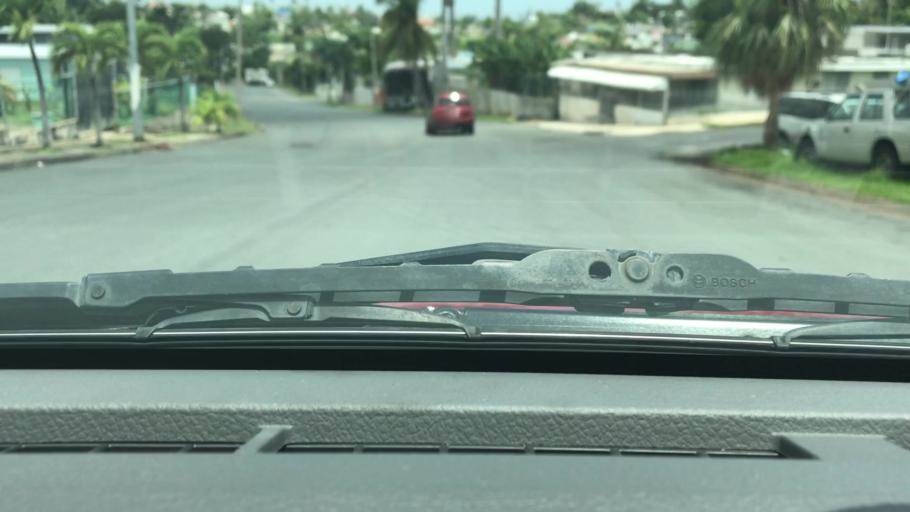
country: PR
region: Toa Alta
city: Pajaros
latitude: 18.3553
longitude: -66.1909
